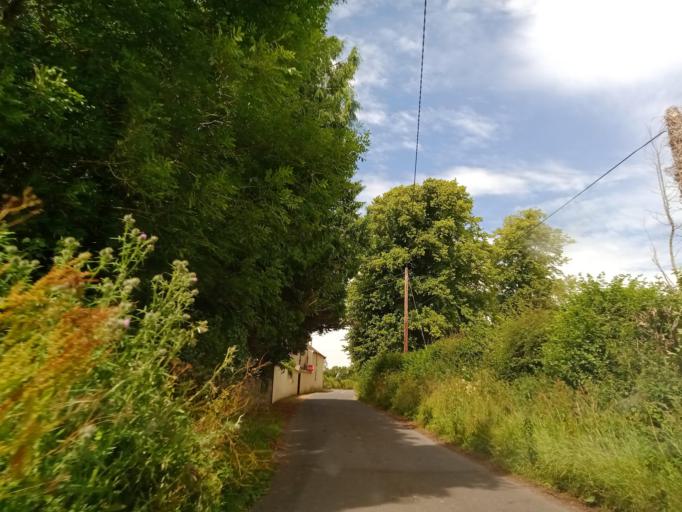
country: IE
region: Leinster
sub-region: Kilkenny
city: Thomastown
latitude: 52.5783
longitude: -7.1268
